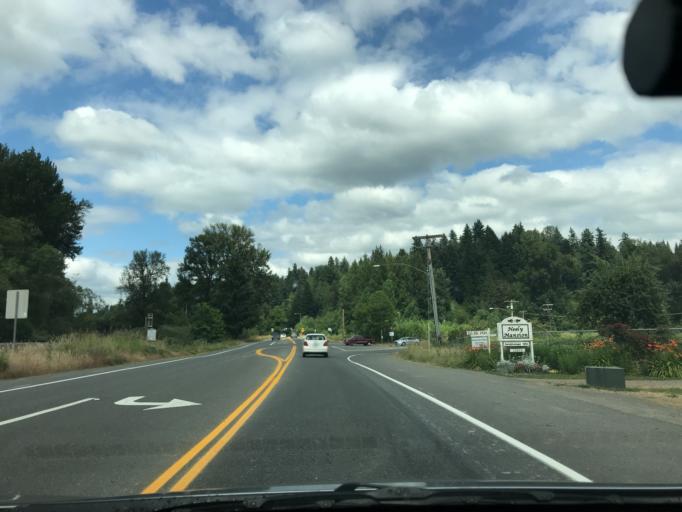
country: US
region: Washington
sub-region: King County
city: Lea Hill
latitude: 47.3006
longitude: -122.1783
